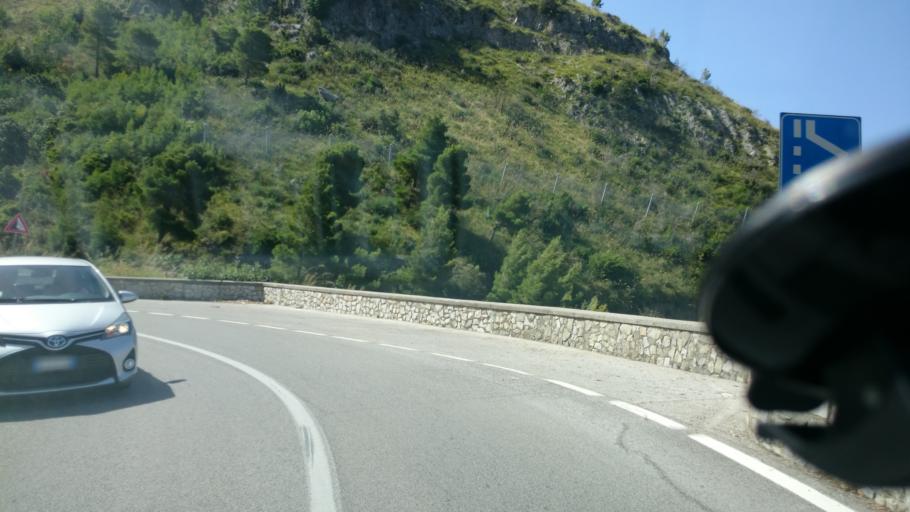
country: IT
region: Basilicate
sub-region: Provincia di Potenza
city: Maratea
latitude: 40.0278
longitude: 15.6794
